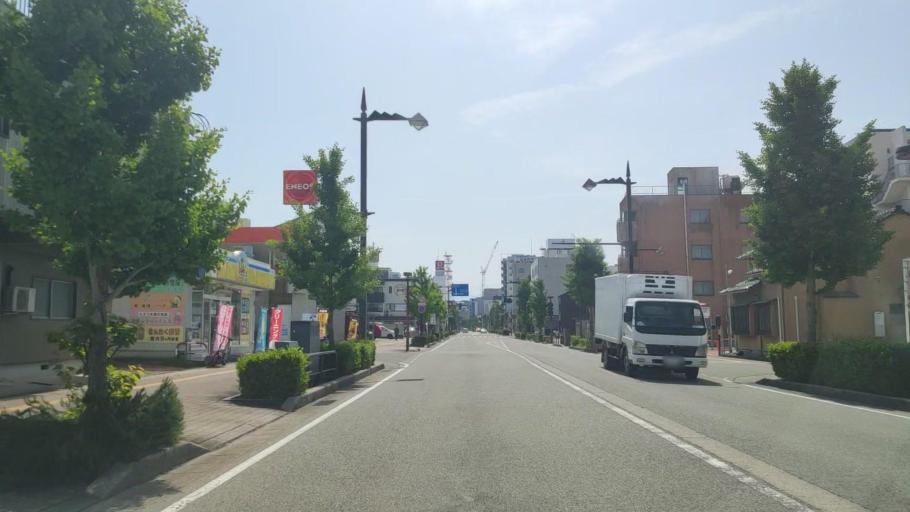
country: JP
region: Toyama
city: Toyama-shi
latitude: 36.6996
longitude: 137.2082
